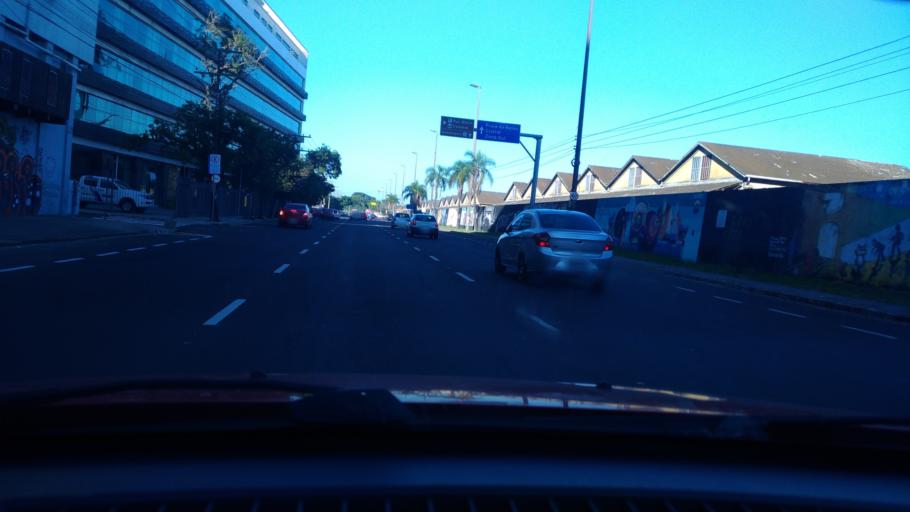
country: BR
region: Rio Grande do Sul
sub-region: Porto Alegre
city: Porto Alegre
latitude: -30.0293
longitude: -51.2350
